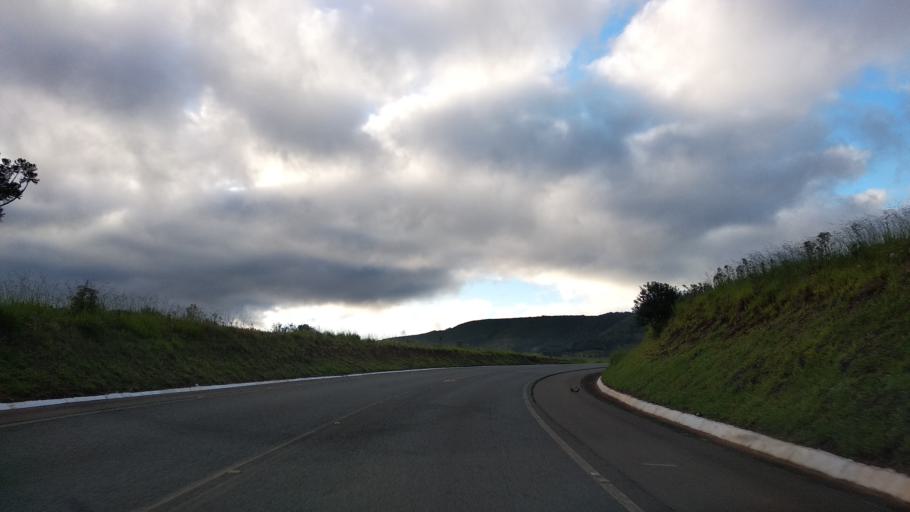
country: BR
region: Santa Catarina
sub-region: Curitibanos
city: Curitibanos
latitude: -27.5685
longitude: -50.8115
